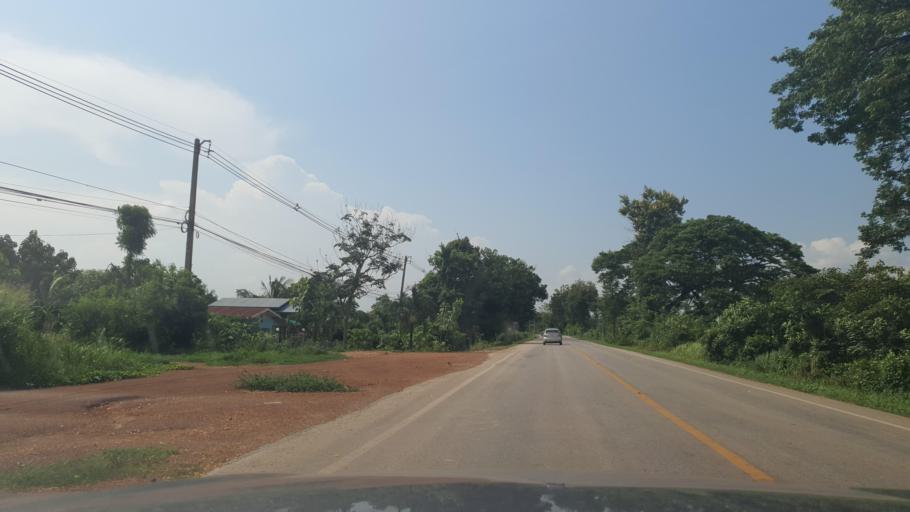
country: TH
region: Sukhothai
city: Si Samrong
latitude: 17.1867
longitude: 99.8517
